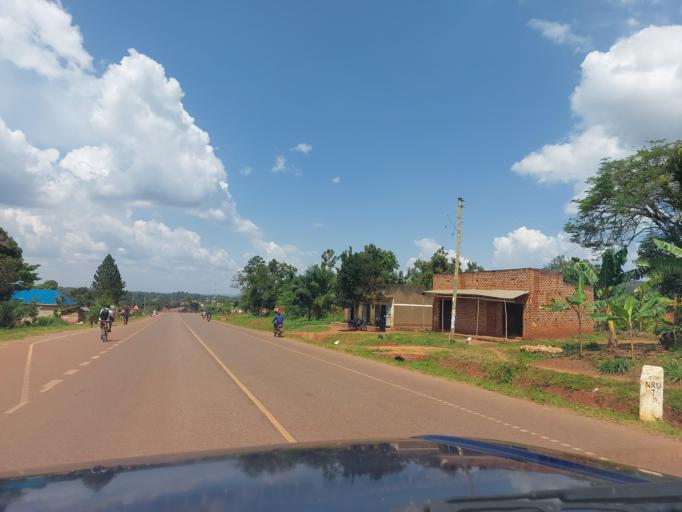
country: UG
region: Central Region
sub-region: Buikwe District
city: Njeru
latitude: 0.3860
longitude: 33.1616
